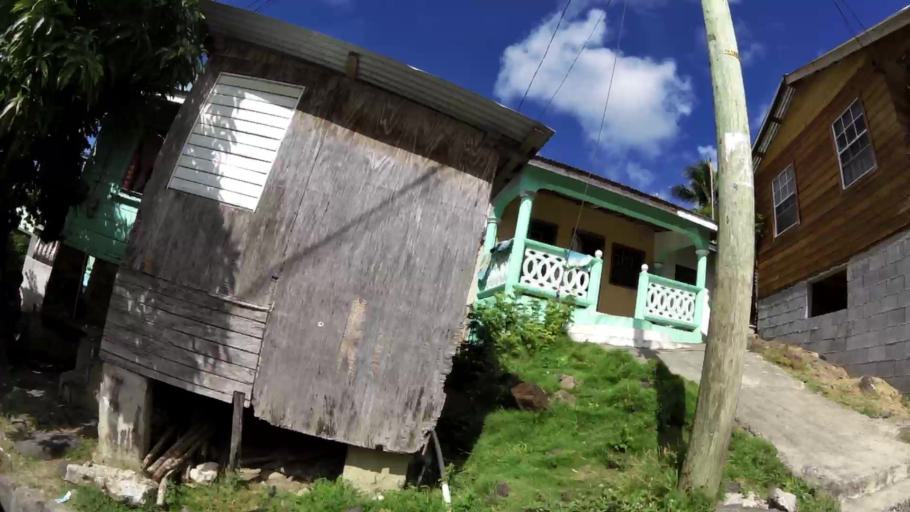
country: LC
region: Laborie Quarter
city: Laborie
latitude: 13.7523
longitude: -60.9949
